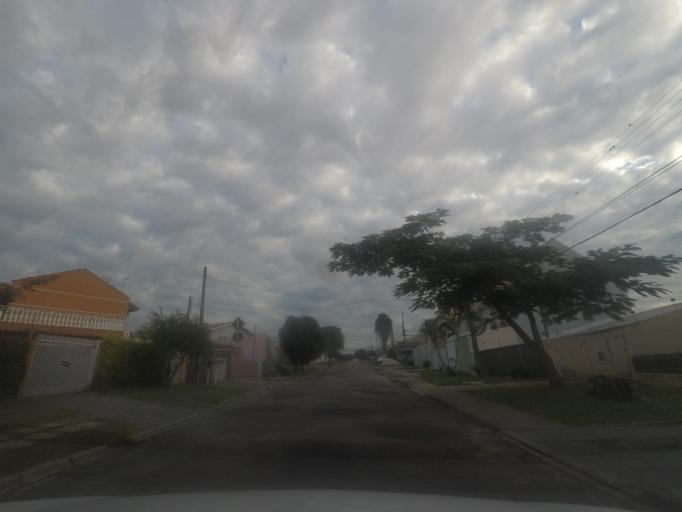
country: BR
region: Parana
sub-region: Pinhais
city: Pinhais
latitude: -25.4674
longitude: -49.2116
